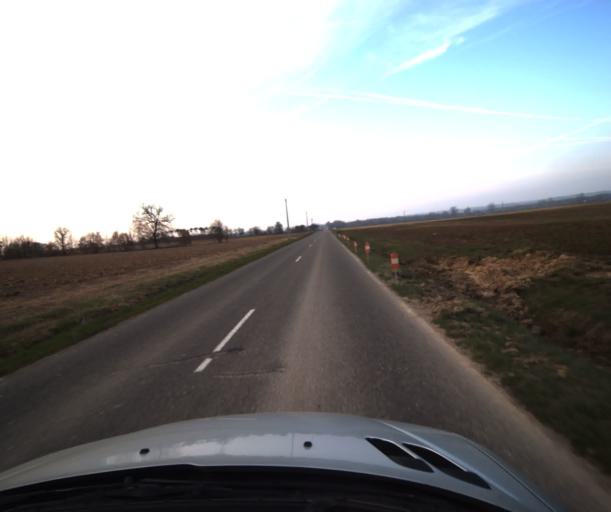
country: FR
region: Midi-Pyrenees
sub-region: Departement du Tarn-et-Garonne
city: Labastide-Saint-Pierre
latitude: 43.8924
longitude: 1.3730
